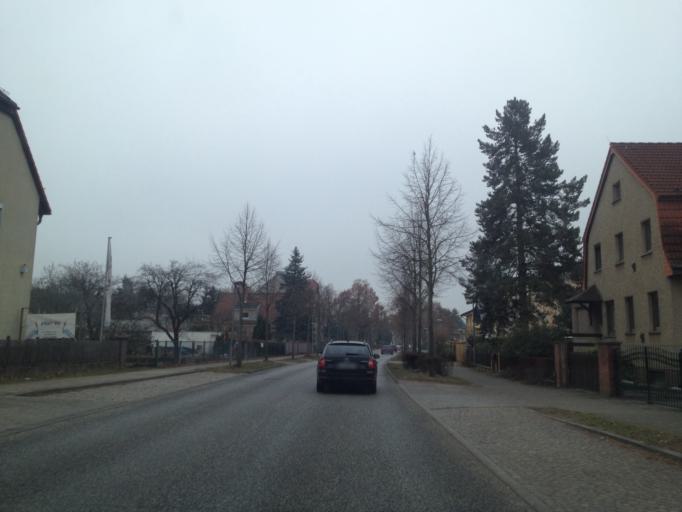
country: DE
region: Berlin
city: Blankenfelde
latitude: 52.6457
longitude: 13.3766
